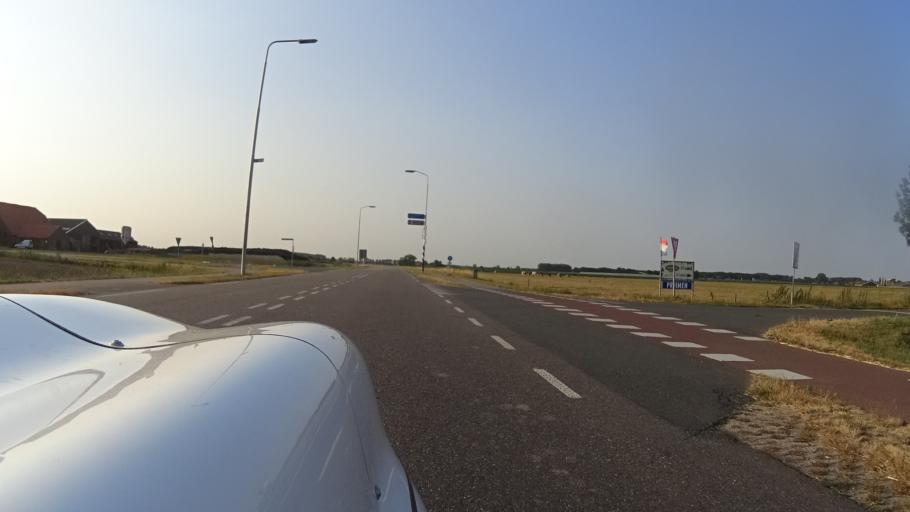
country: NL
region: Gelderland
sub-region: Gemeente Druten
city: Druten
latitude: 51.8415
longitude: 5.5845
